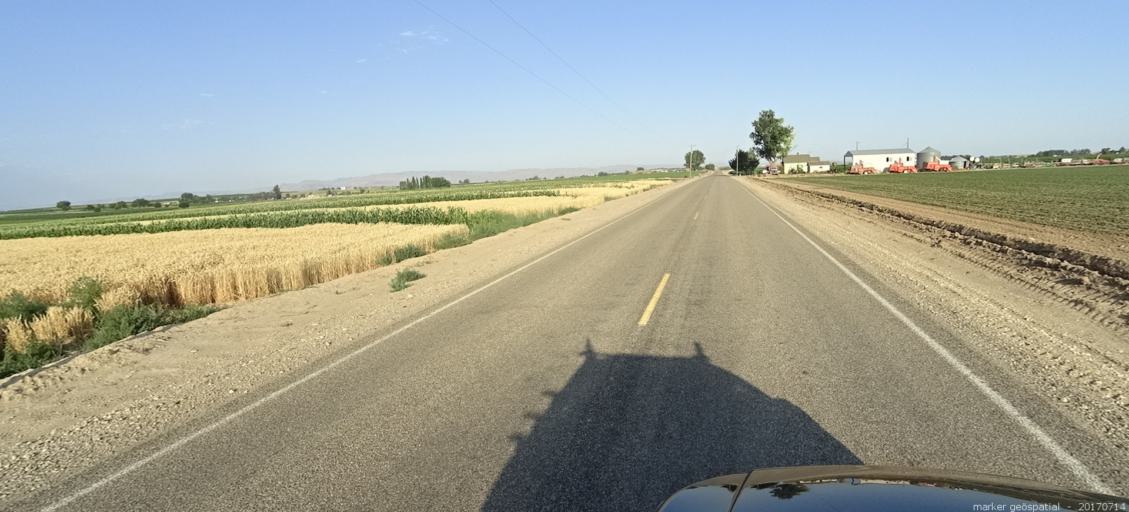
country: US
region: Idaho
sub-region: Ada County
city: Kuna
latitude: 43.4593
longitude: -116.5009
